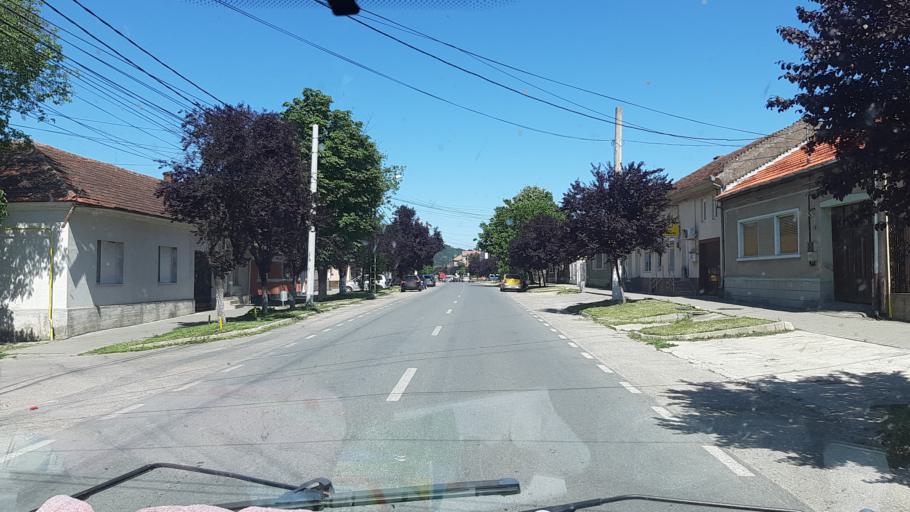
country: RO
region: Caras-Severin
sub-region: Oras Bocsa
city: Bocsa
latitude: 45.3763
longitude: 21.7178
